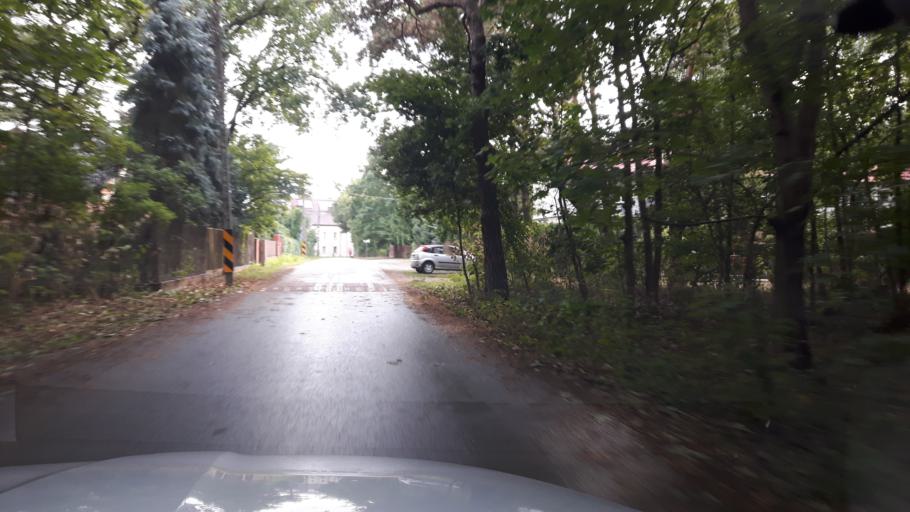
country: PL
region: Masovian Voivodeship
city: Zielonka
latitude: 52.3160
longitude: 21.1559
